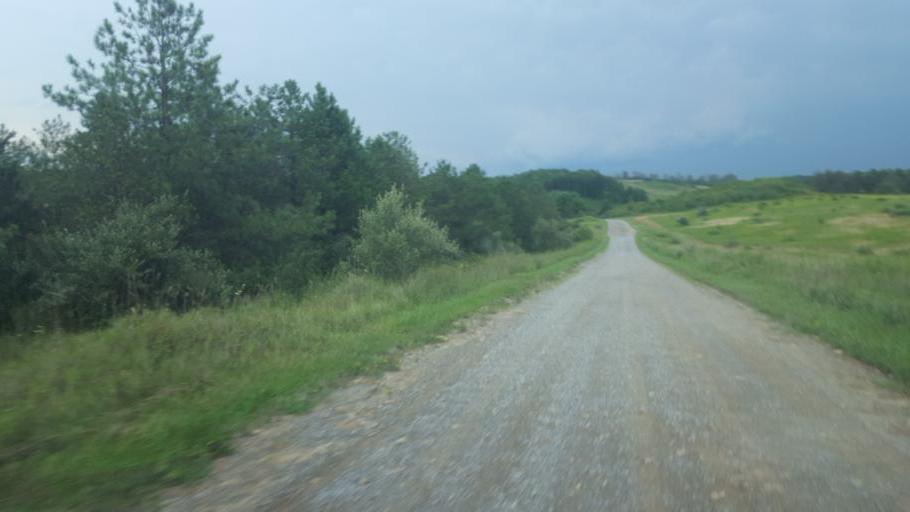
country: US
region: Pennsylvania
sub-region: Clarion County
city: Knox
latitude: 41.1473
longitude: -79.4963
